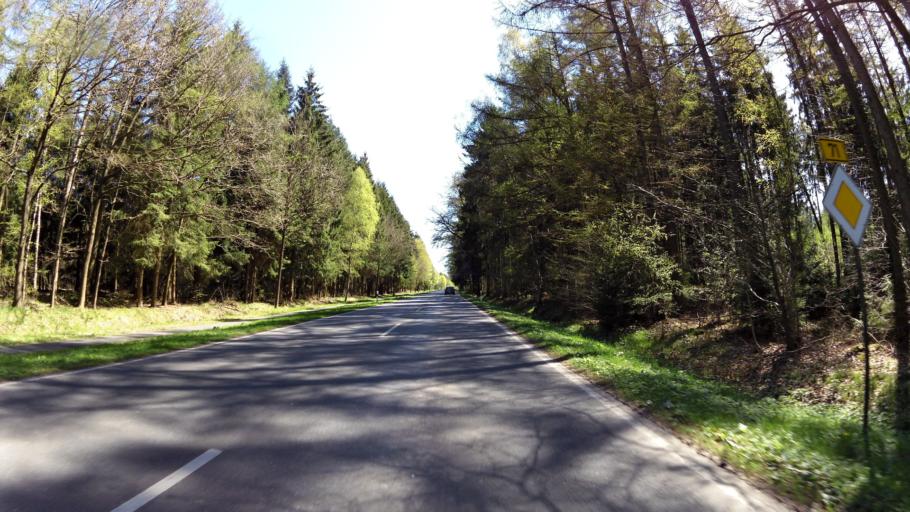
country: DE
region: Lower Saxony
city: Soltau
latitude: 53.0107
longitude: 9.7895
